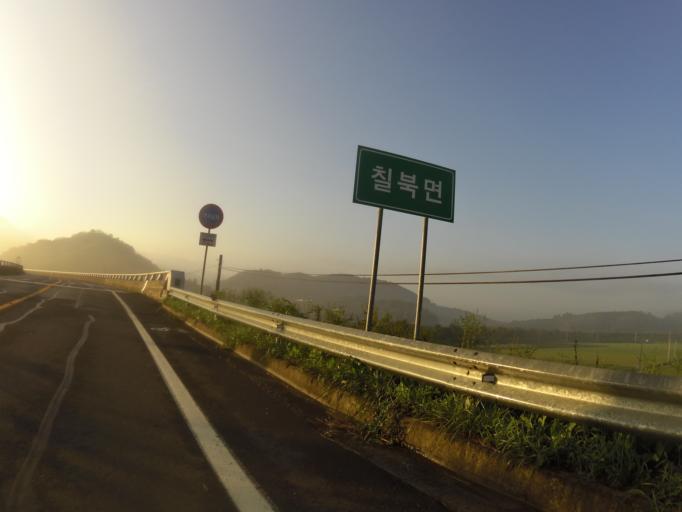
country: KR
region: Gyeongsangnam-do
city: Naeso
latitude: 35.3825
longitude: 128.5202
